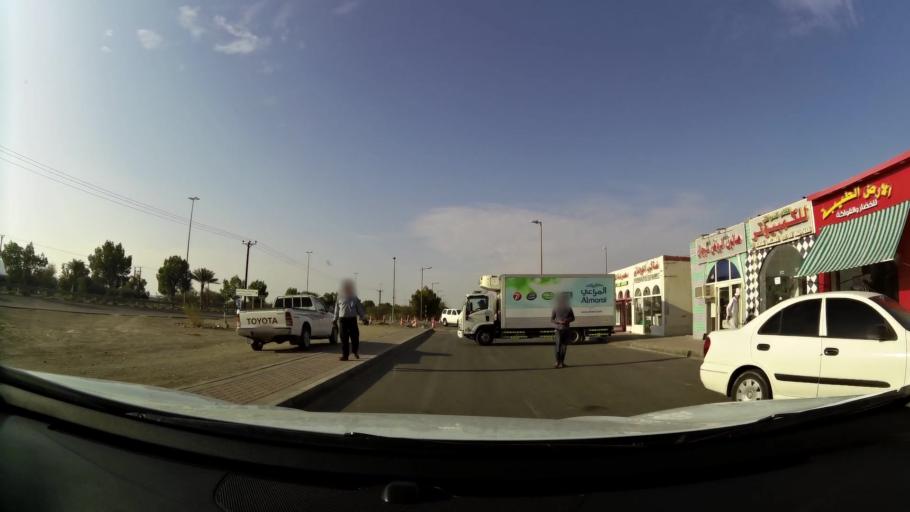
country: AE
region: Abu Dhabi
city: Al Ain
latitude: 24.0791
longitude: 55.8340
